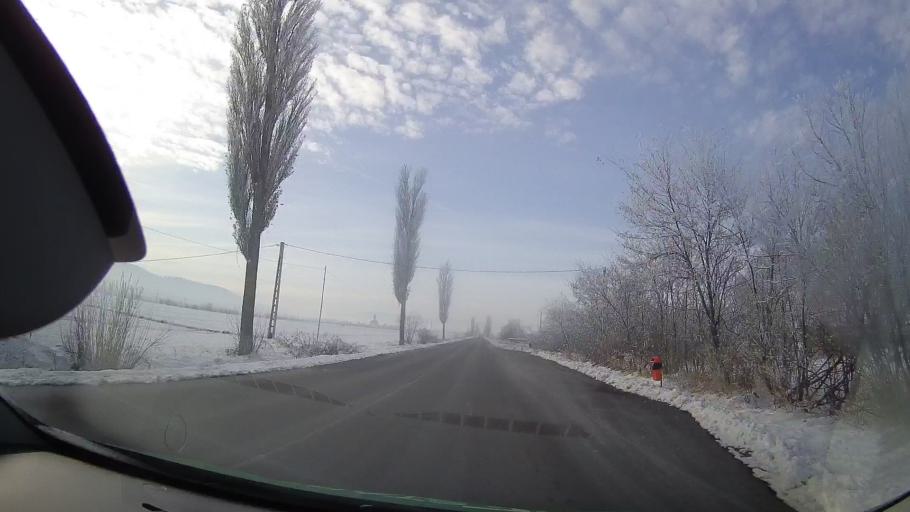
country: RO
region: Neamt
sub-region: Comuna Timisesti
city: Dumbrava
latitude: 47.2168
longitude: 26.4473
